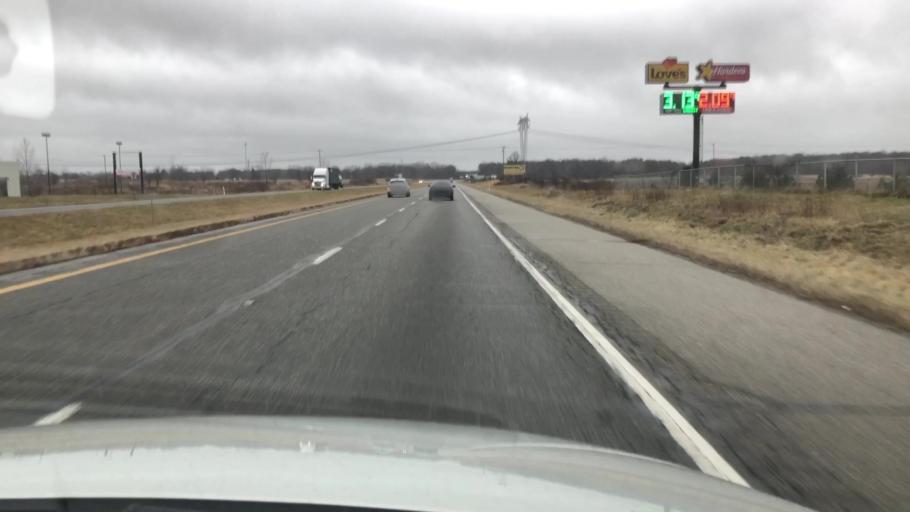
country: US
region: Indiana
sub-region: Marshall County
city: Plymouth
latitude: 41.3615
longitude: -86.3517
